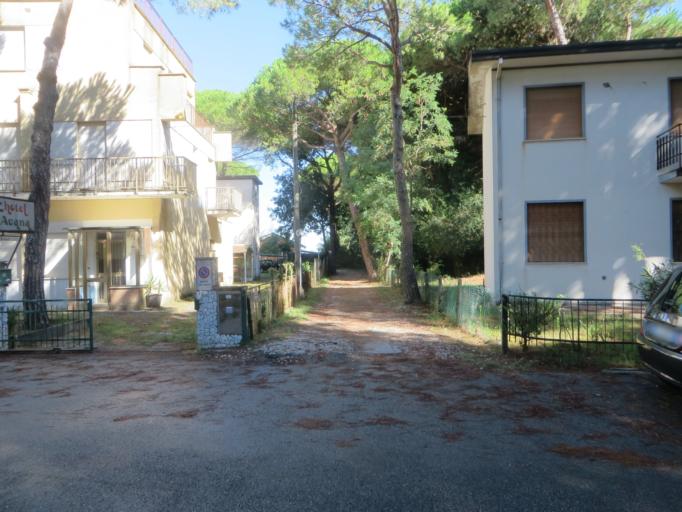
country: IT
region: Veneto
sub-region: Provincia di Venezia
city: Eraclea
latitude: 45.5291
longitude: 12.7156
